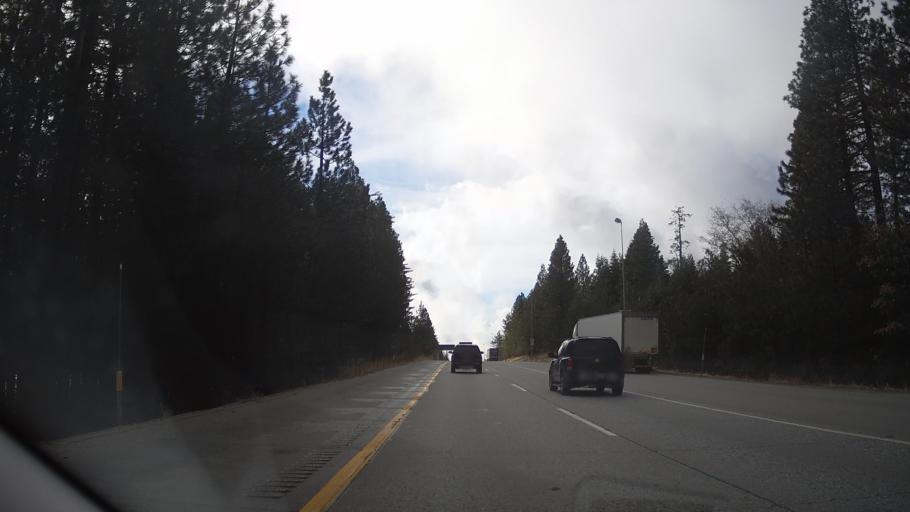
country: US
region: California
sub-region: Placer County
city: Foresthill
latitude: 39.2886
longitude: -120.6945
